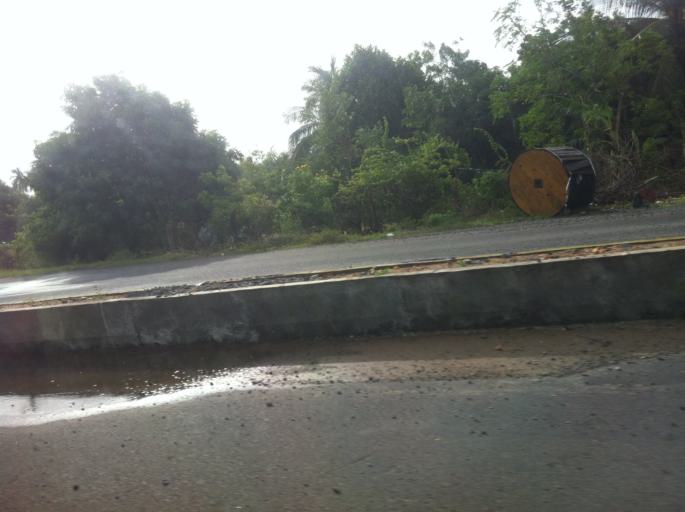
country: IN
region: Tamil Nadu
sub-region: Kancheepuram
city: Cheyyur
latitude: 12.3181
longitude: 80.0308
